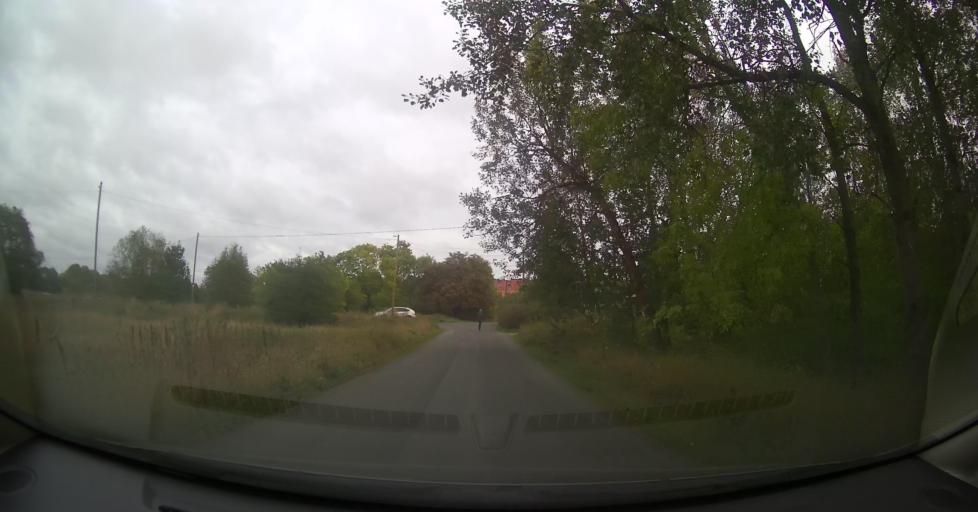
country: EE
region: Harju
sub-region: Tallinna linn
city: Kose
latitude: 59.4470
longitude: 24.8353
